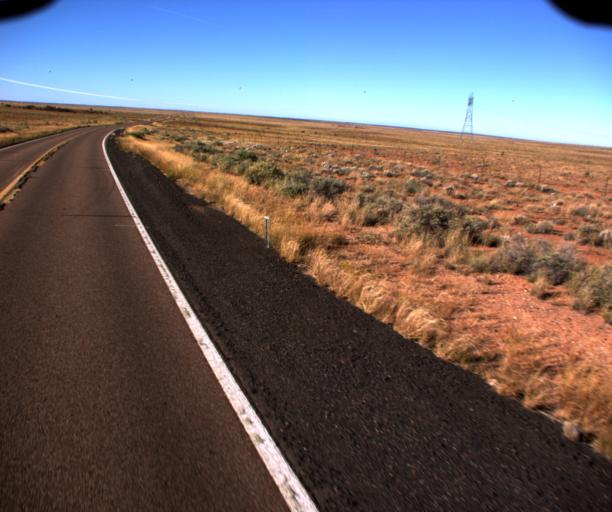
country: US
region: Arizona
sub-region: Navajo County
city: Holbrook
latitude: 34.7977
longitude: -110.2122
